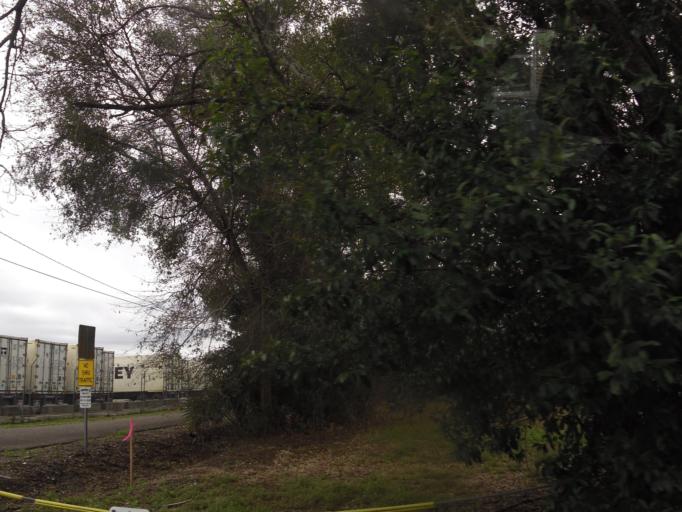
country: US
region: Florida
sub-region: Duval County
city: Jacksonville
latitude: 30.3568
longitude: -81.6313
